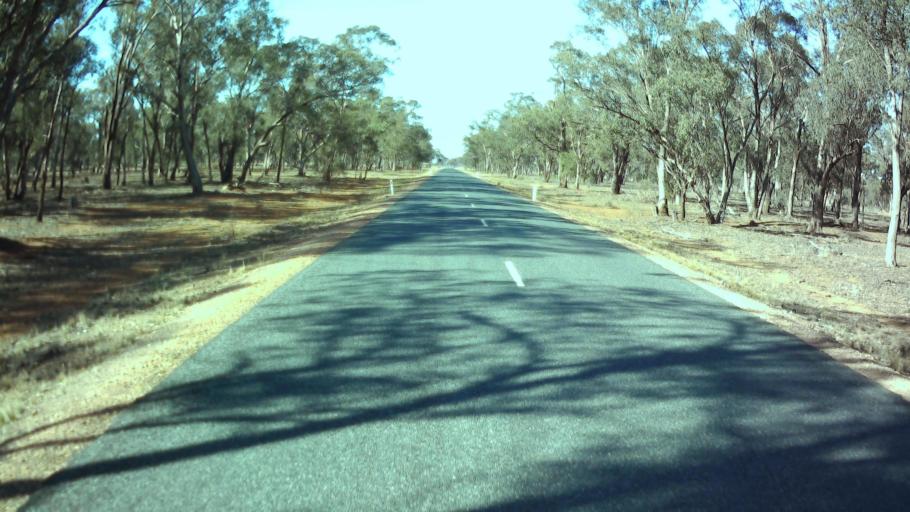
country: AU
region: New South Wales
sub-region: Weddin
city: Grenfell
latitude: -34.0635
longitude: 147.9083
